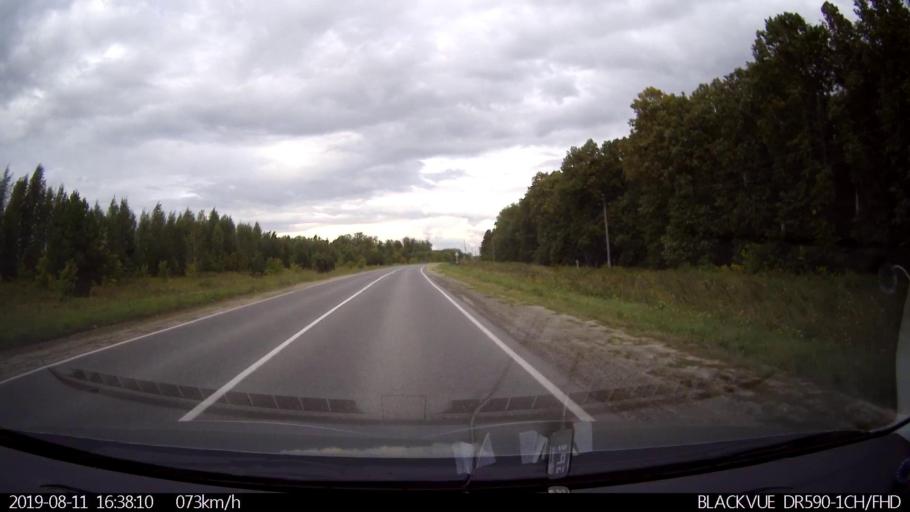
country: RU
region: Ulyanovsk
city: Mayna
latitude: 54.1331
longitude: 47.6218
